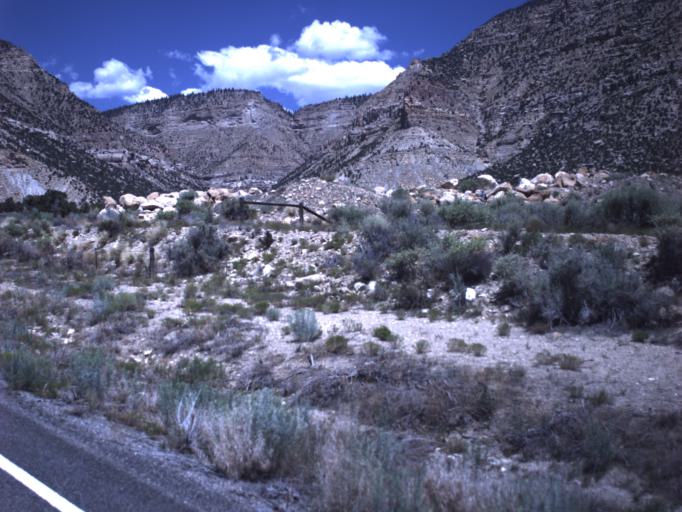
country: US
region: Utah
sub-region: Emery County
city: Orangeville
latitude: 39.2974
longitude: -111.1153
